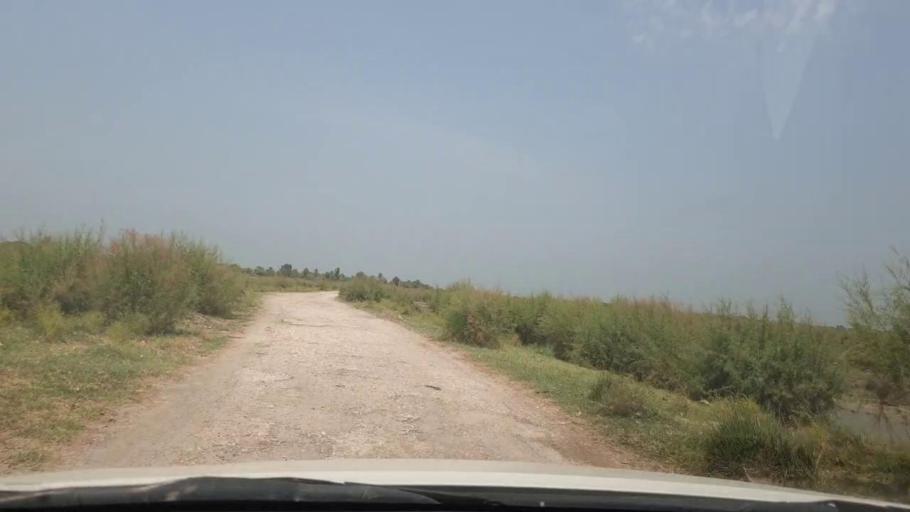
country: PK
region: Sindh
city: Rustam jo Goth
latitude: 28.0542
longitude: 68.7521
